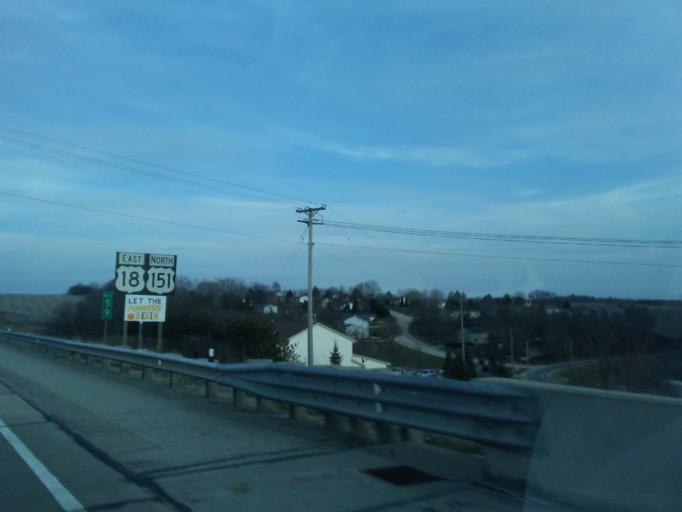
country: US
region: Wisconsin
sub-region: Iowa County
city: Barneveld
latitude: 43.0103
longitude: -89.8912
